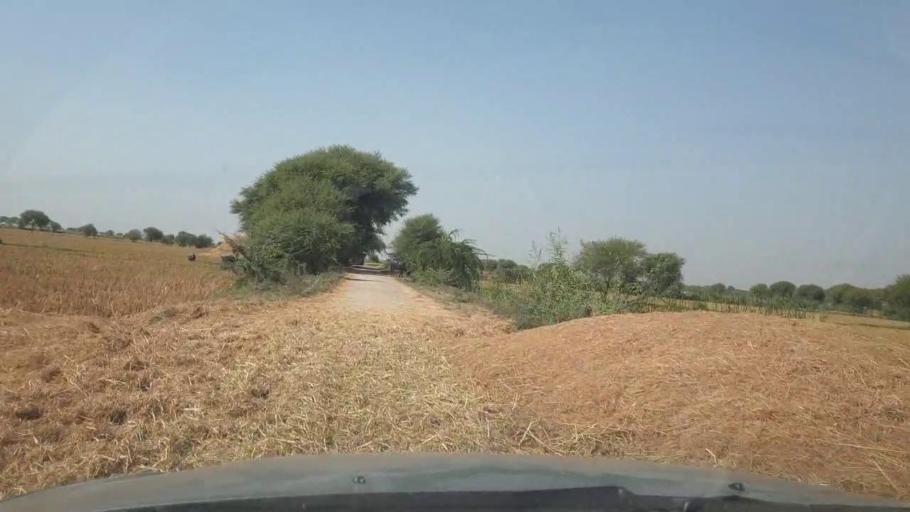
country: PK
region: Sindh
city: Bulri
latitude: 24.8720
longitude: 68.4487
